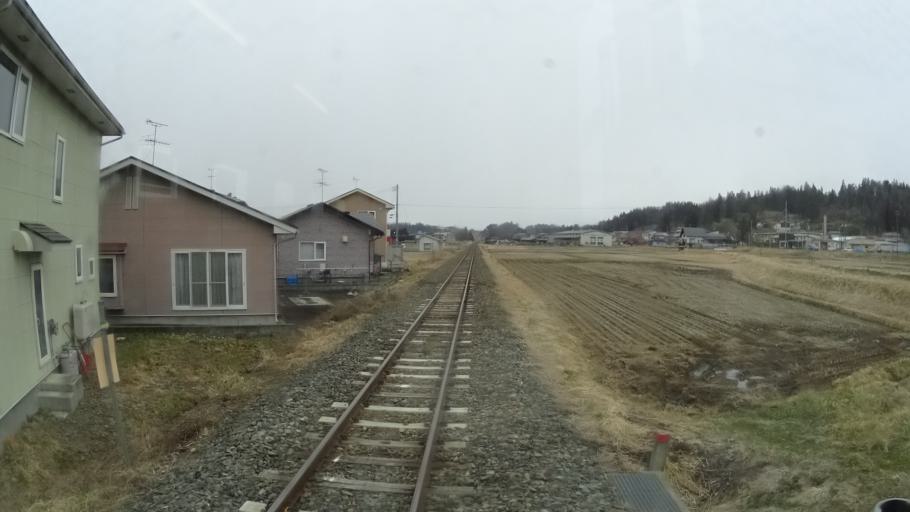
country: JP
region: Iwate
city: Hanamaki
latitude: 39.3798
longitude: 141.2381
